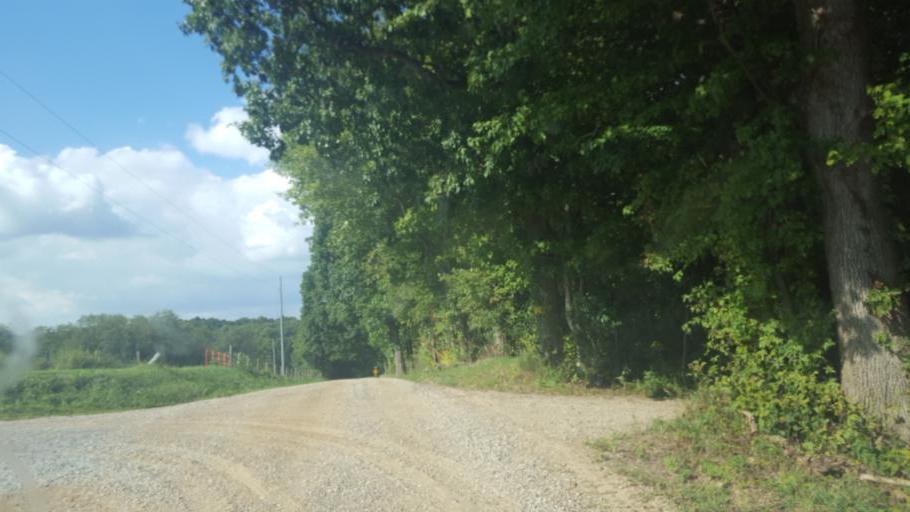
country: US
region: Ohio
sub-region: Knox County
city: Danville
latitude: 40.4541
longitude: -82.3081
